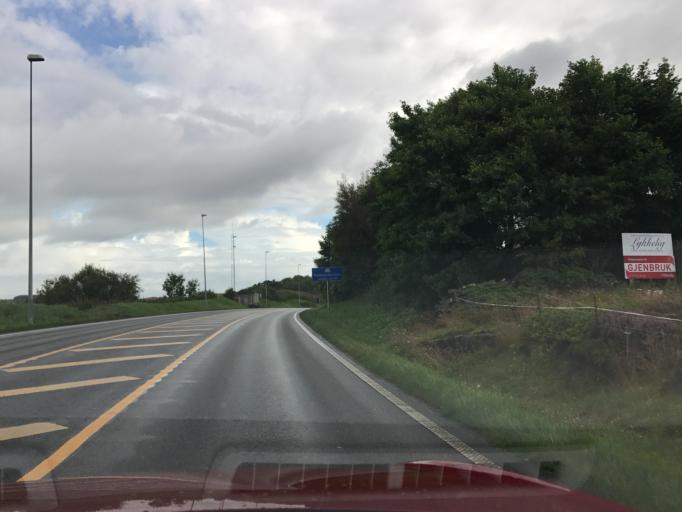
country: NO
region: Rogaland
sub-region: Rennesoy
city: Vikevag
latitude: 59.0699
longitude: 5.6737
